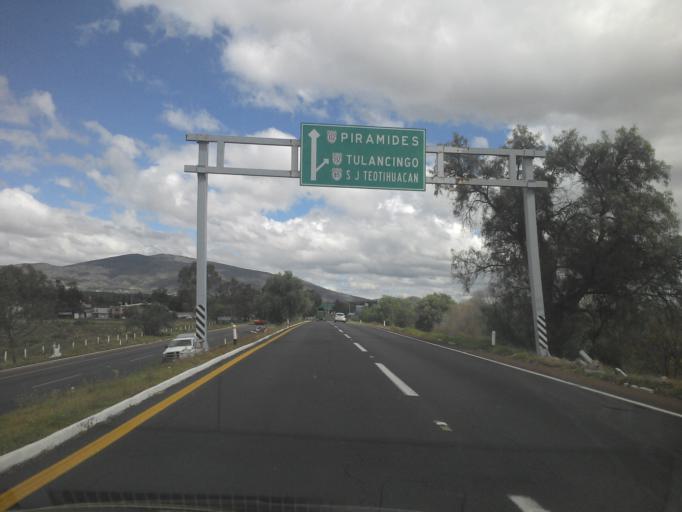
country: MX
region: Morelos
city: Teotihuacan de Arista
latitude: 19.6749
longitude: -98.8637
